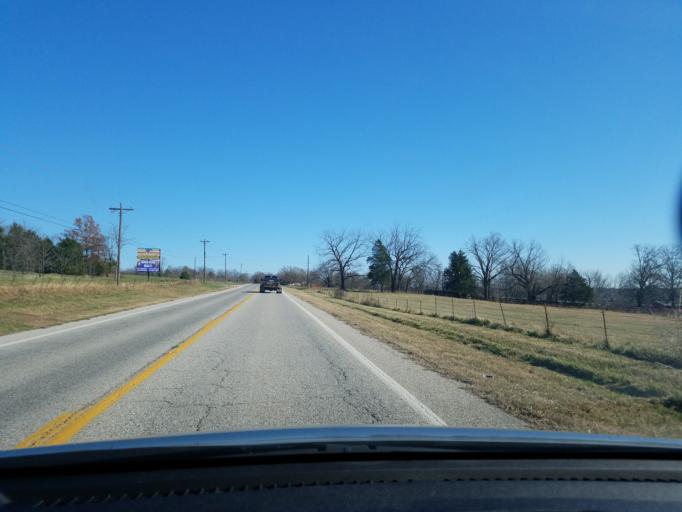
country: US
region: Arkansas
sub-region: Carroll County
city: Eureka Springs
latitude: 36.3978
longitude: -93.6499
